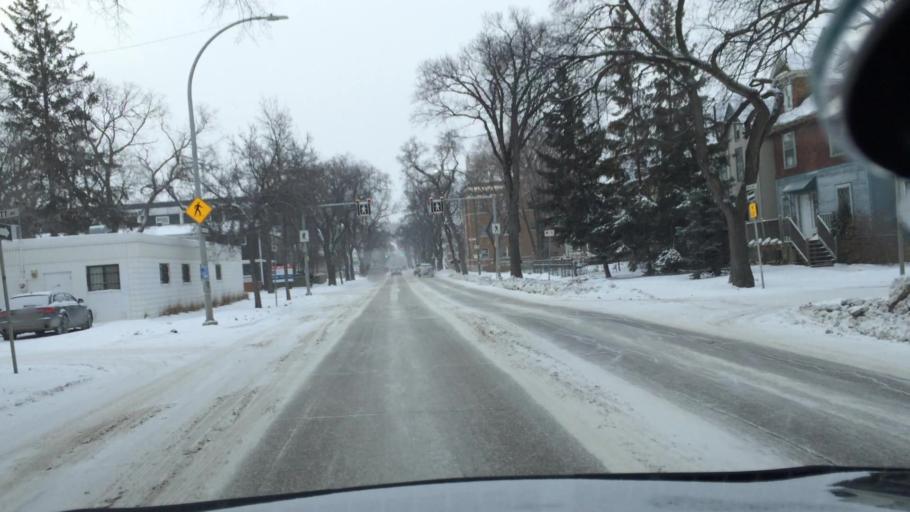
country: CA
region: Manitoba
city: Winnipeg
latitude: 49.8845
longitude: -97.1608
